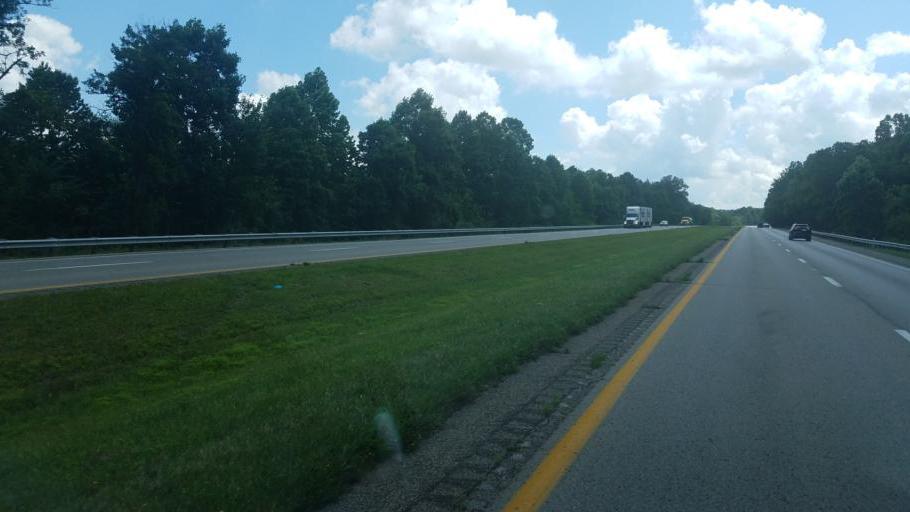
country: US
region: Ohio
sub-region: Jackson County
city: Jackson
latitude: 39.0271
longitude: -82.5879
